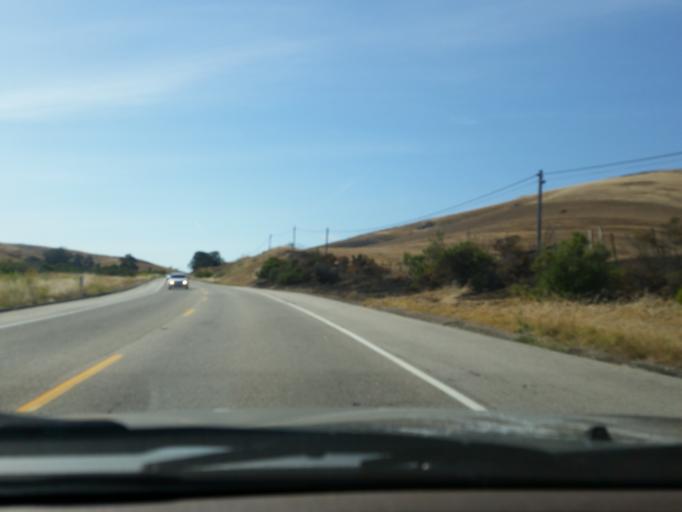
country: US
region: California
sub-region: San Luis Obispo County
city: Cambria
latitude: 35.4945
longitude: -121.0049
